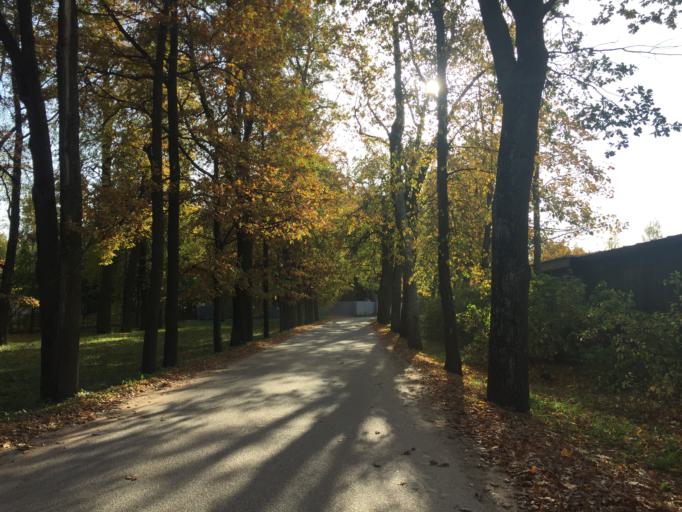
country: RU
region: St.-Petersburg
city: Pushkin
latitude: 59.7152
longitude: 30.3850
